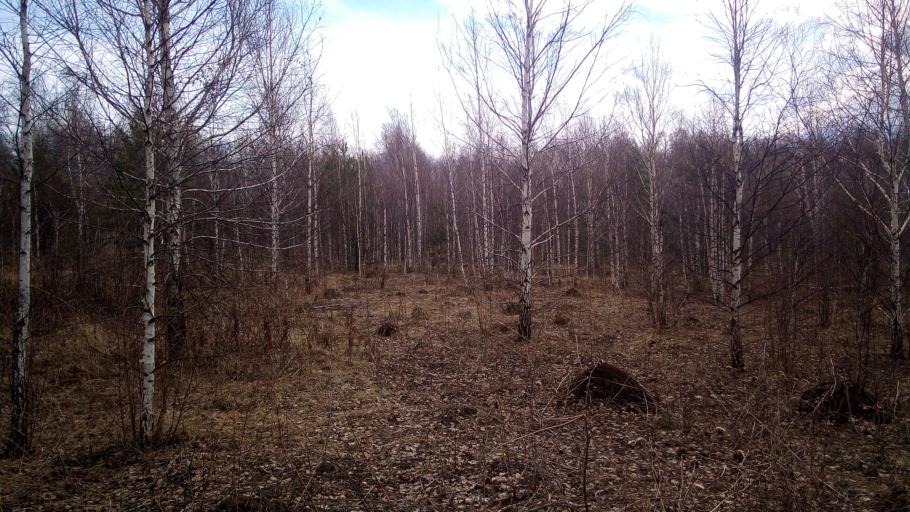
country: RU
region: Chelyabinsk
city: Sargazy
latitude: 55.1239
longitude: 61.2500
